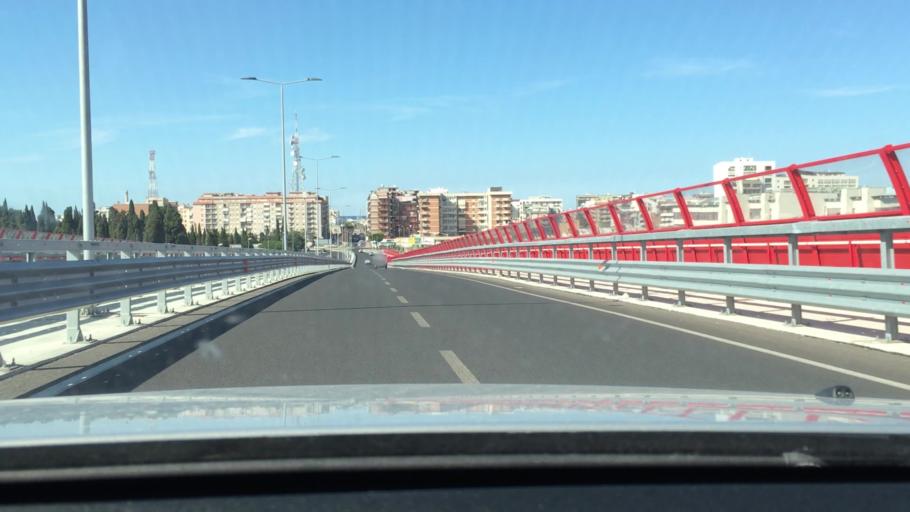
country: IT
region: Apulia
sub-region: Provincia di Bari
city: Bari
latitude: 41.1209
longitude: 16.8482
